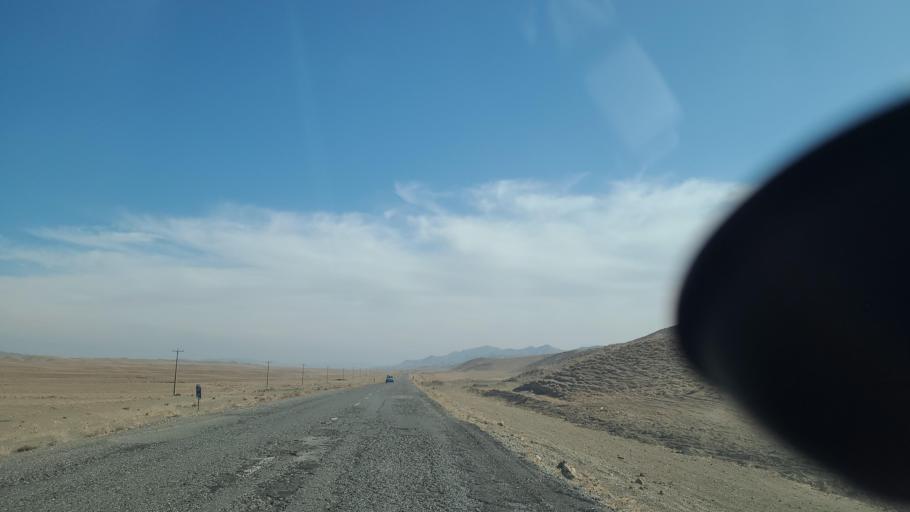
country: IR
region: Razavi Khorasan
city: Fariman
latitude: 35.5913
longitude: 59.6047
